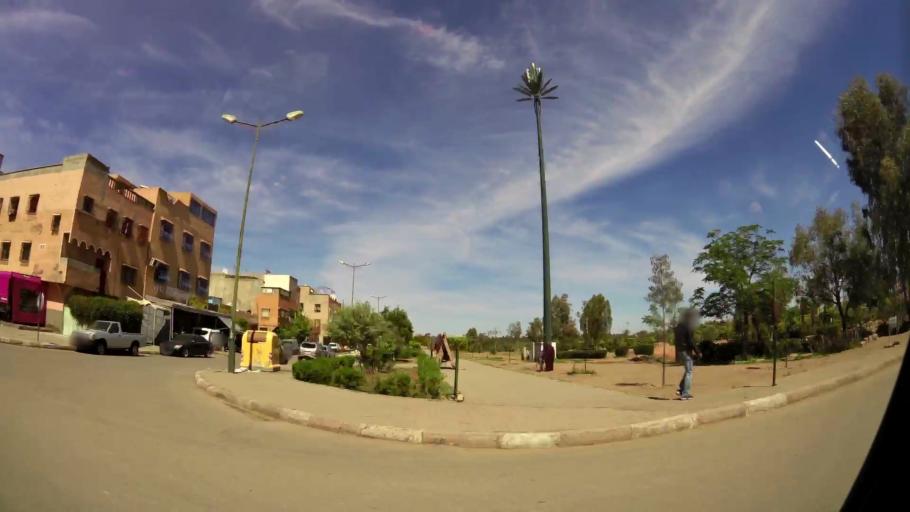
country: MA
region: Marrakech-Tensift-Al Haouz
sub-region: Marrakech
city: Marrakesh
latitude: 31.6038
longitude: -7.9620
